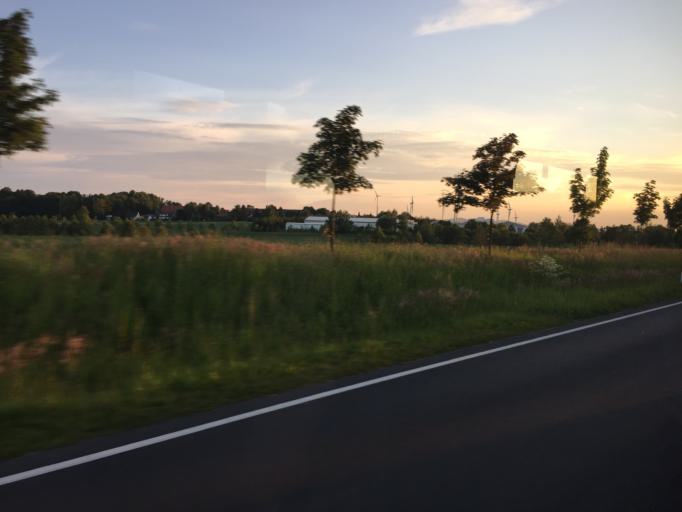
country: DE
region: Saxony
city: Reichenbach
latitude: 51.1496
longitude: 14.8016
